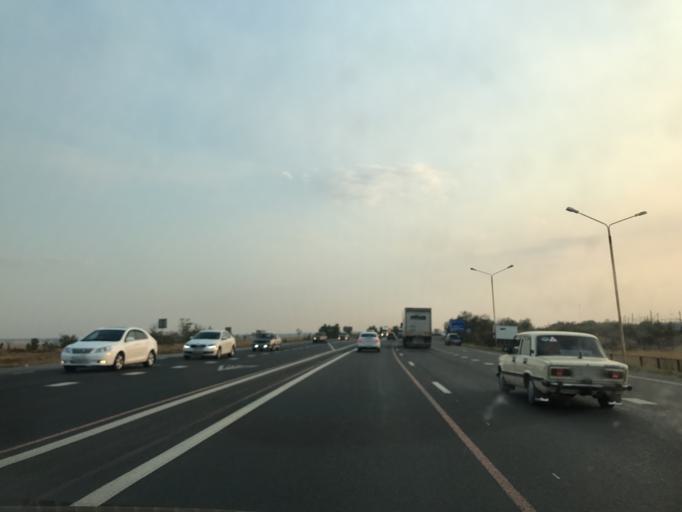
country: RU
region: Rostov
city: Kamensk-Shakhtinskiy
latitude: 48.2499
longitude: 40.2917
